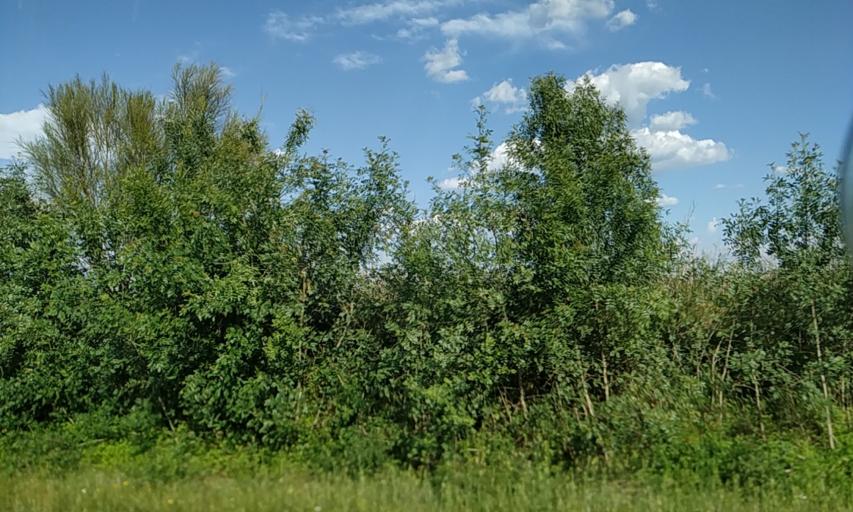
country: PT
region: Evora
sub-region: Estremoz
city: Estremoz
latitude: 38.9699
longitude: -7.4923
